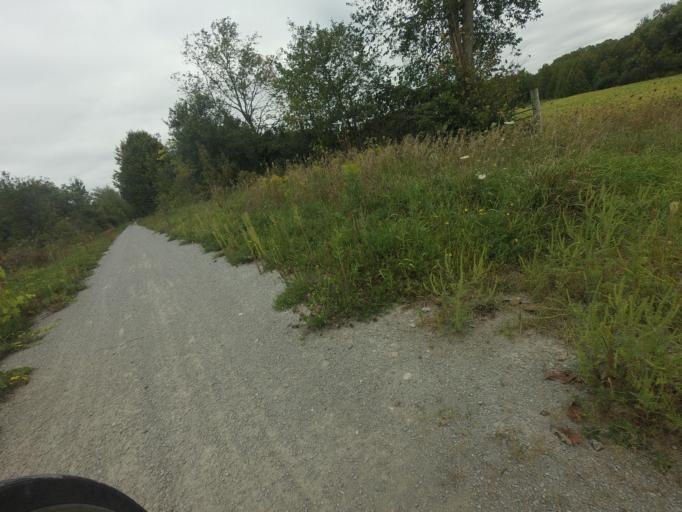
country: CA
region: Ontario
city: Omemee
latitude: 44.3227
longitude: -78.8264
